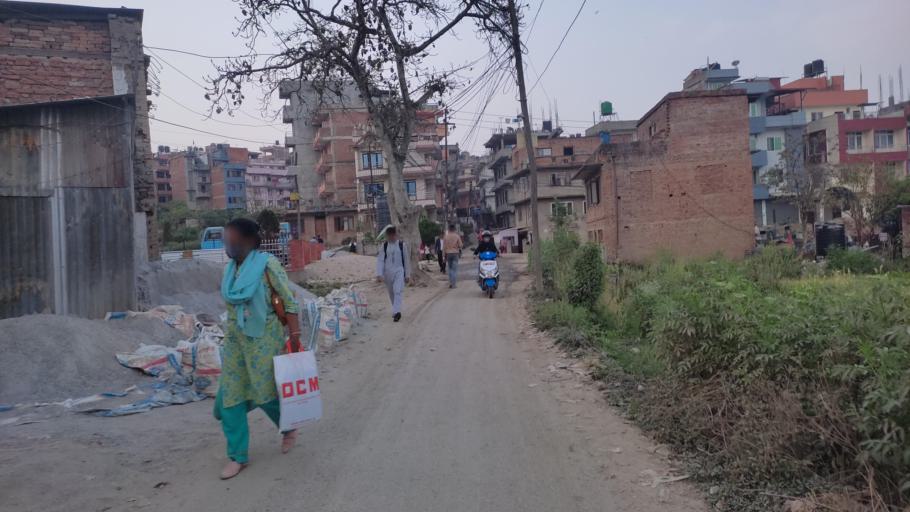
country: NP
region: Central Region
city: Kirtipur
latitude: 27.6676
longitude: 85.2786
